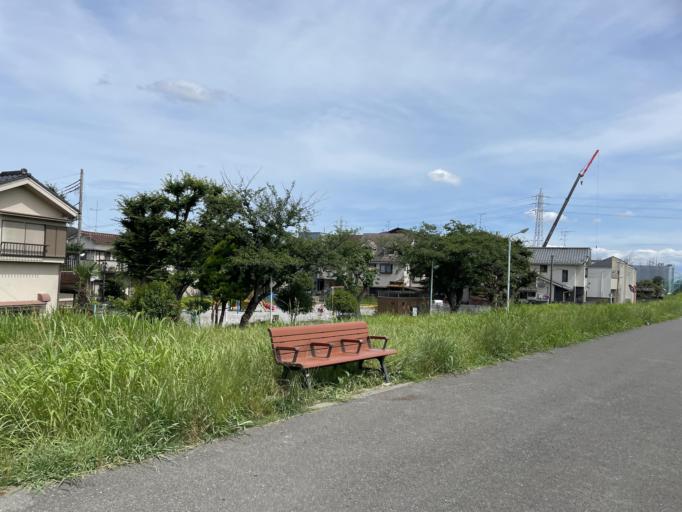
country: JP
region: Chiba
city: Matsudo
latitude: 35.7553
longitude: 139.8597
